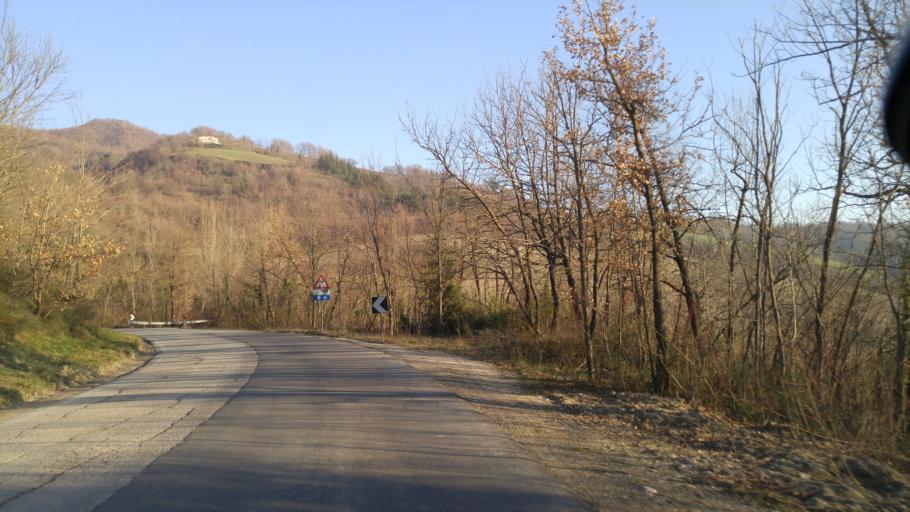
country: IT
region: The Marches
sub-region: Provincia di Pesaro e Urbino
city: Fermignano
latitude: 43.6614
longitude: 12.6618
